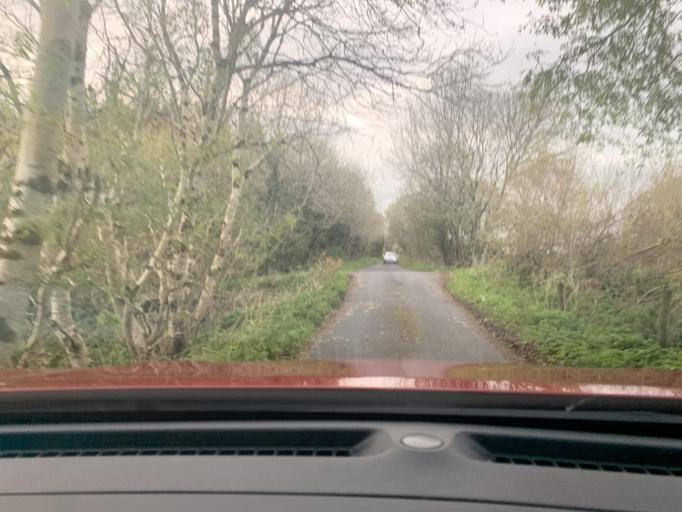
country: IE
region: Connaught
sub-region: Sligo
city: Tobercurry
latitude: 54.0198
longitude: -8.6328
